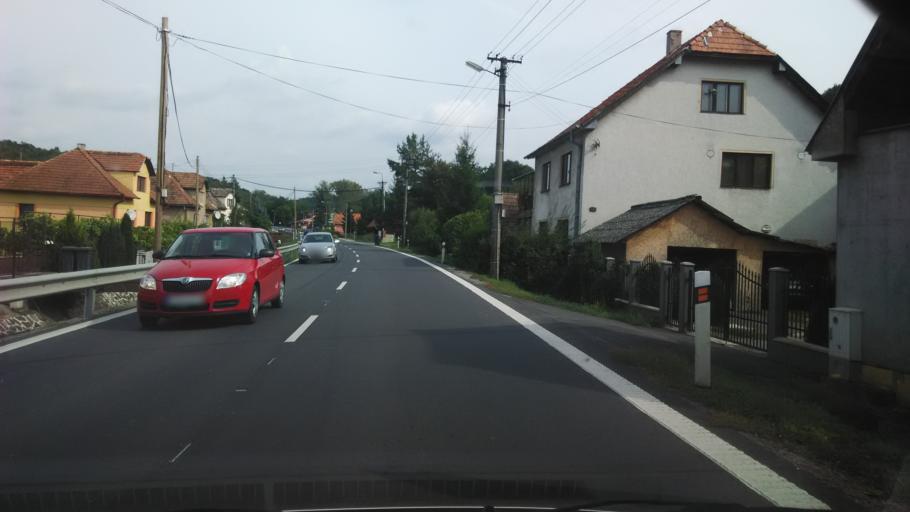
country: SK
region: Banskobystricky
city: Krupina
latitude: 48.2888
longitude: 19.0039
